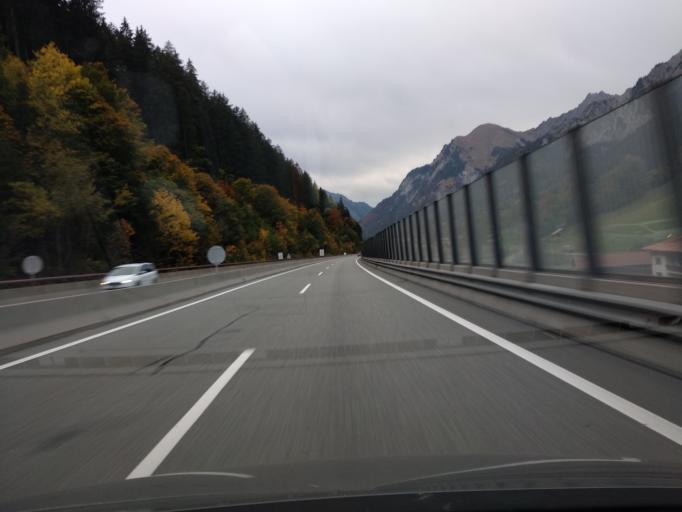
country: AT
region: Vorarlberg
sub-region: Politischer Bezirk Bludenz
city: Klosterle
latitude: 47.1302
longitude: 10.0753
